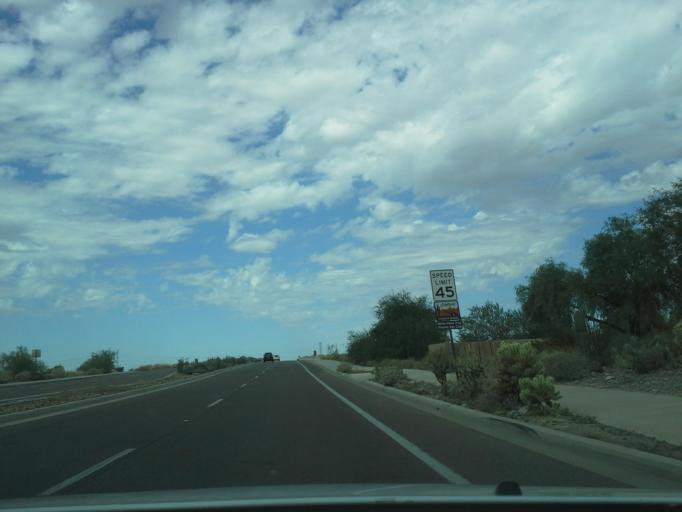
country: US
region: Arizona
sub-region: Maricopa County
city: Paradise Valley
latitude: 33.6402
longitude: -111.8699
